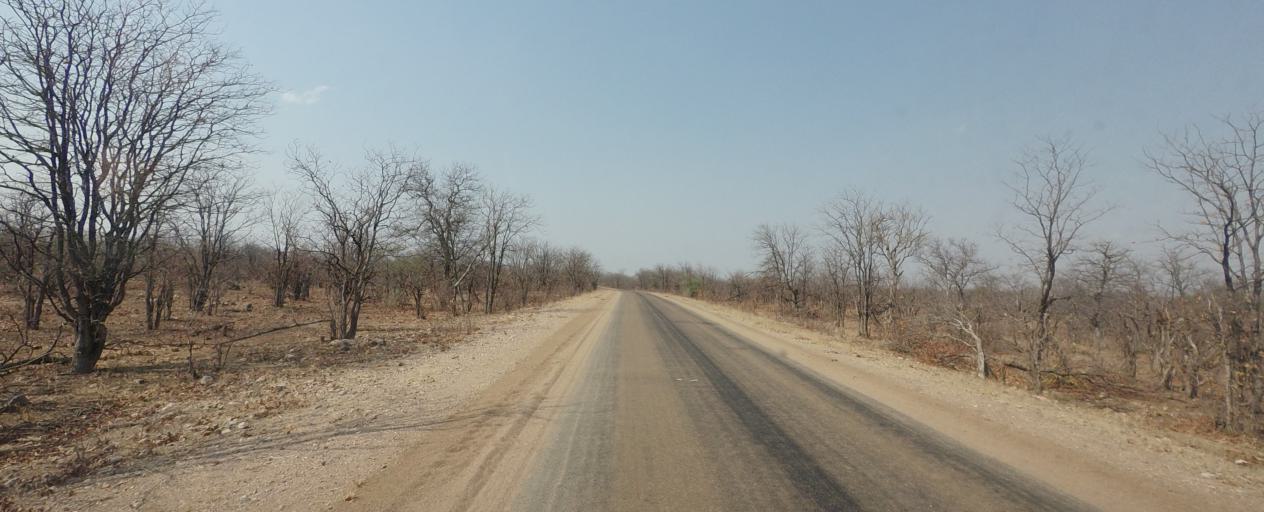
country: ZA
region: Limpopo
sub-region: Mopani District Municipality
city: Giyani
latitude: -23.1932
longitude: 31.3146
